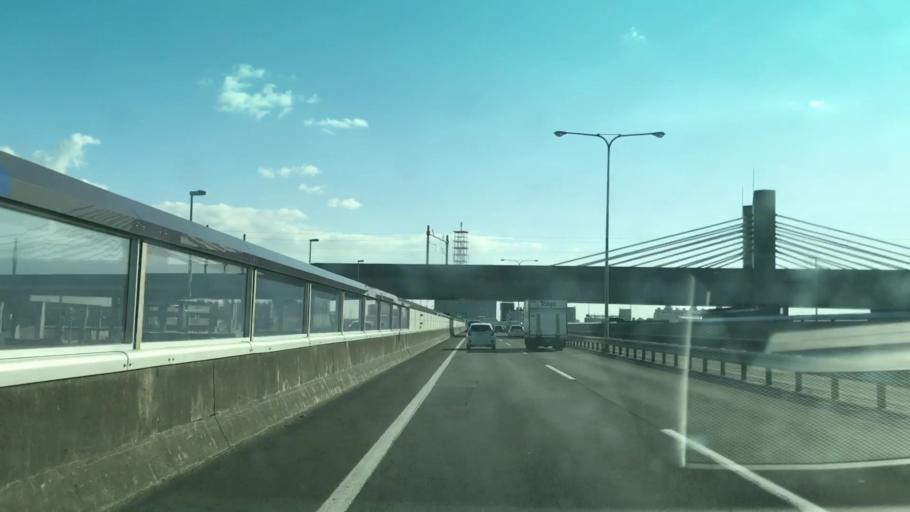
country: JP
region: Hokkaido
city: Sapporo
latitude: 43.1018
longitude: 141.3249
